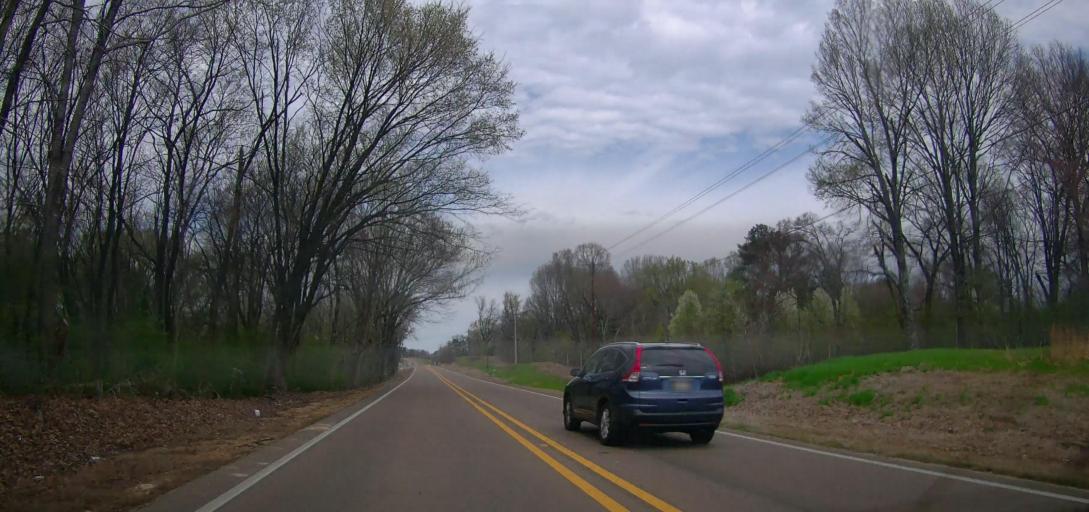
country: US
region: Mississippi
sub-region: De Soto County
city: Olive Branch
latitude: 34.9718
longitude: -89.8396
